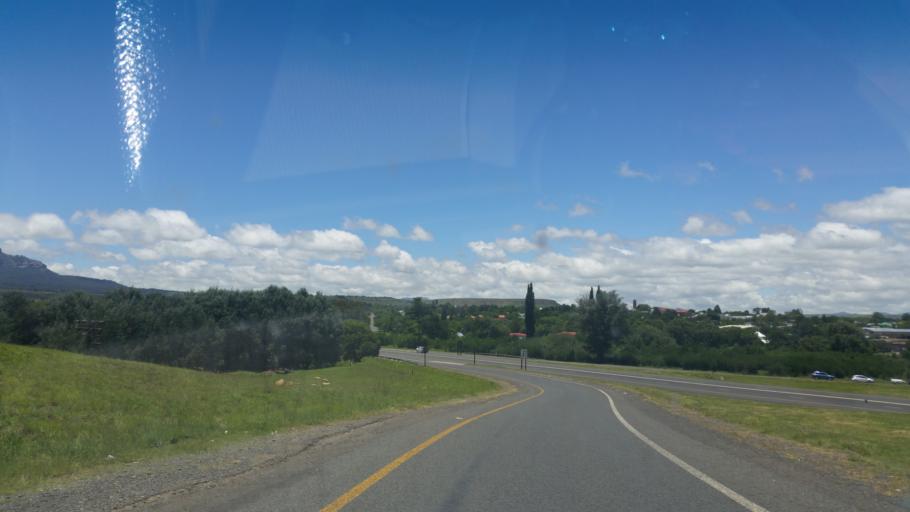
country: ZA
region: Orange Free State
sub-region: Thabo Mofutsanyana District Municipality
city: Harrismith
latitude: -28.2587
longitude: 29.1188
